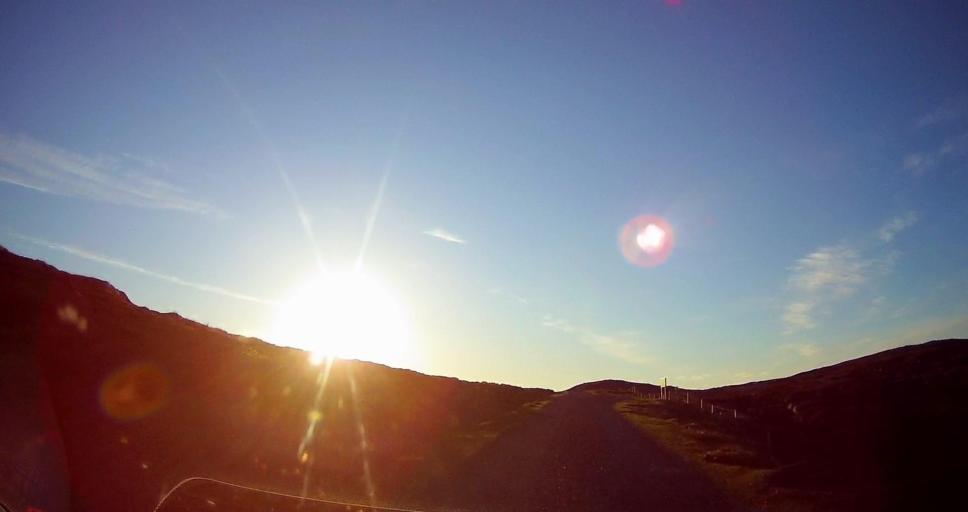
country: GB
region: Scotland
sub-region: Shetland Islands
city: Lerwick
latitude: 60.4414
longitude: -1.4021
